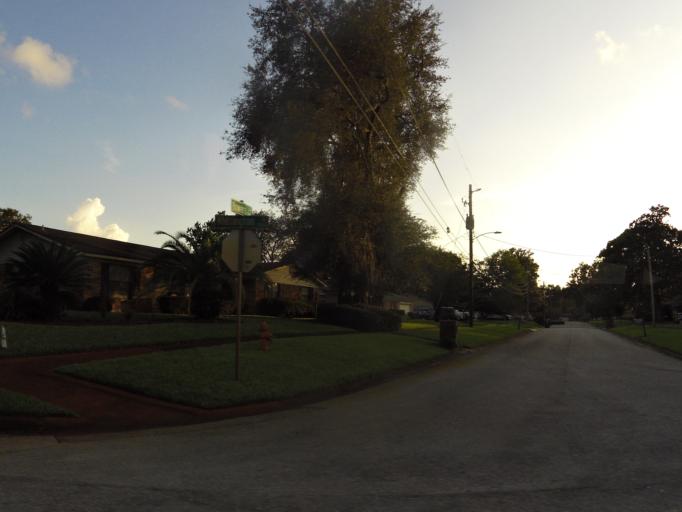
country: US
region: Florida
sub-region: Clay County
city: Orange Park
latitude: 30.2049
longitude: -81.6245
